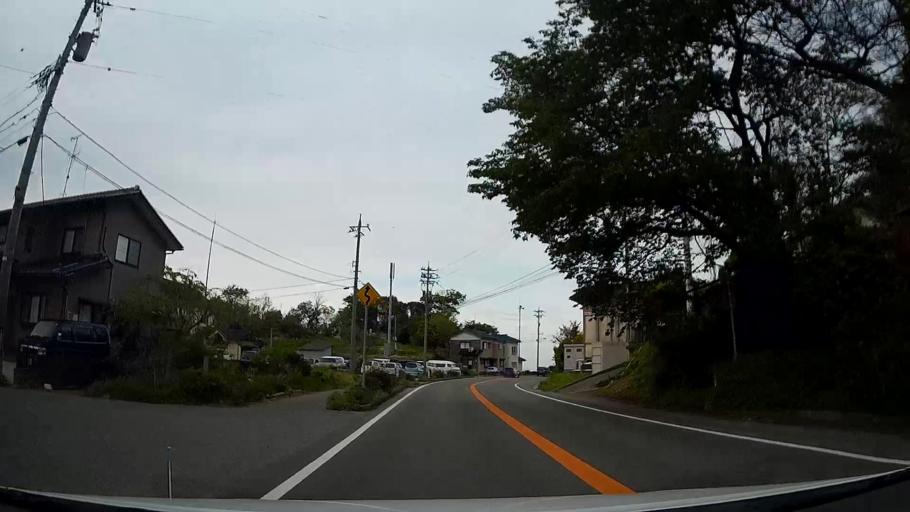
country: JP
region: Ishikawa
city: Nanao
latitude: 37.3989
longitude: 136.9395
